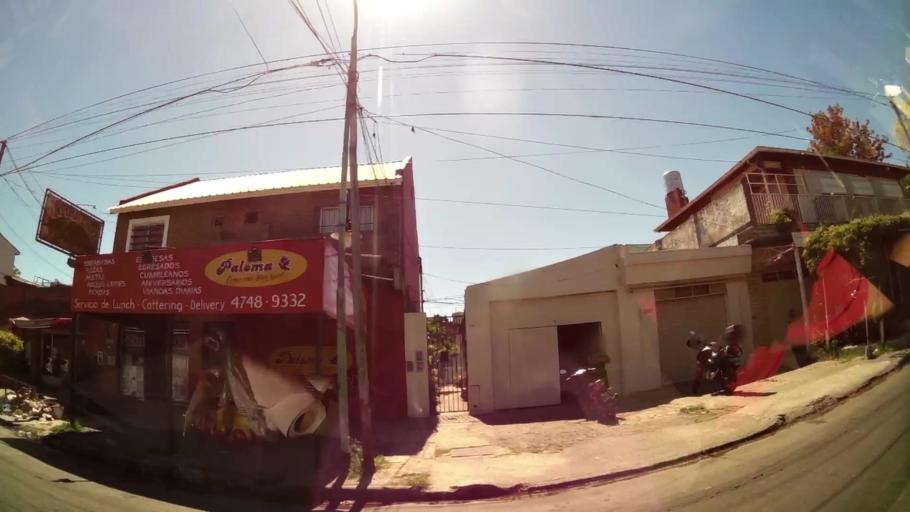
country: AR
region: Buenos Aires
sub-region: Partido de Tigre
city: Tigre
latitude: -34.4957
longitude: -58.6160
